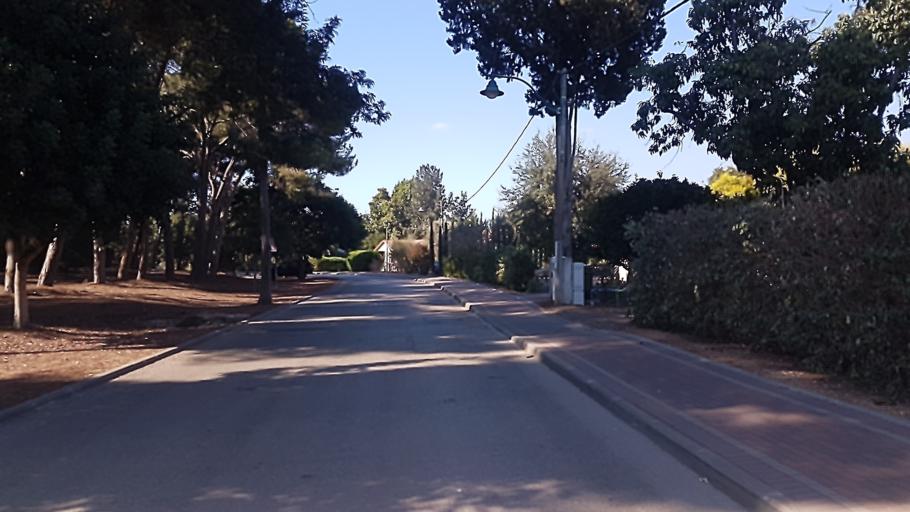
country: IL
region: Central District
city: Kfar Saba
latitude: 32.2105
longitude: 34.9013
